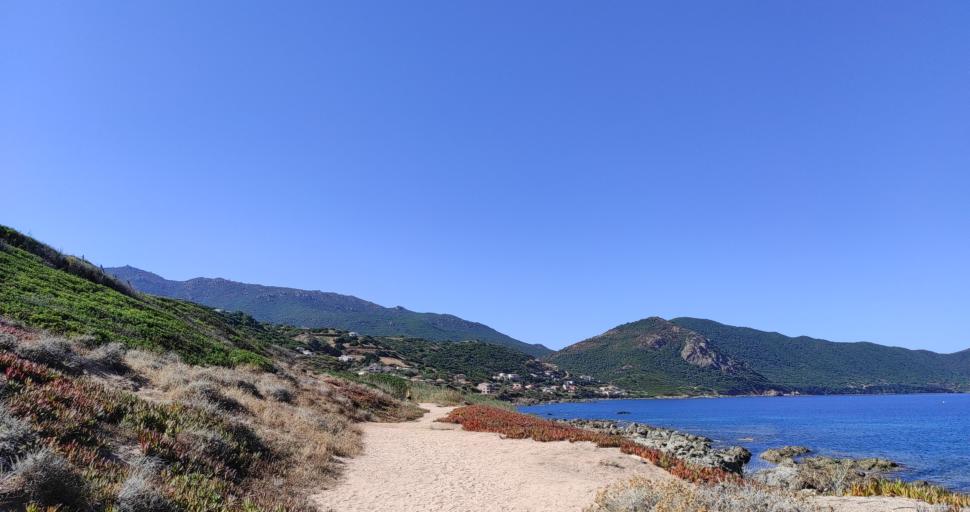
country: FR
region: Corsica
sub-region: Departement de la Corse-du-Sud
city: Alata
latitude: 41.9863
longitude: 8.6703
